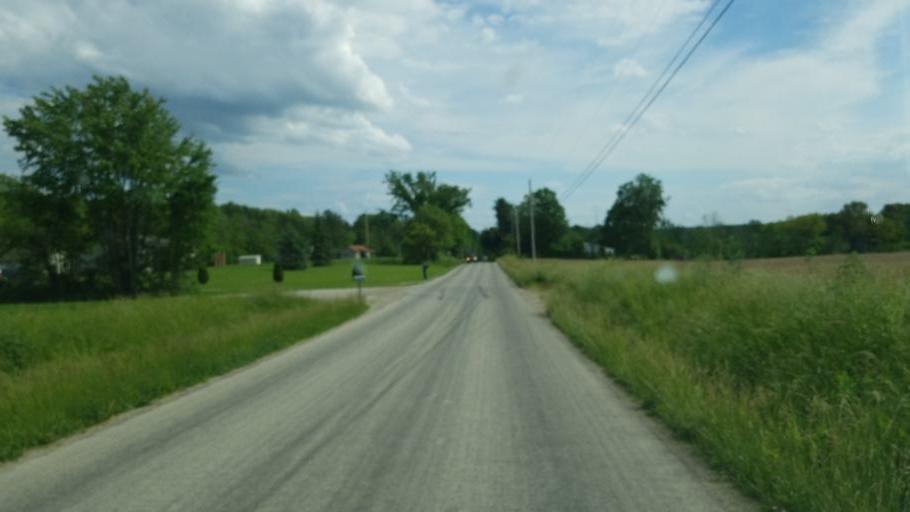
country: US
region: Ohio
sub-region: Huron County
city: Greenwich
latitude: 40.9209
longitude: -82.5326
